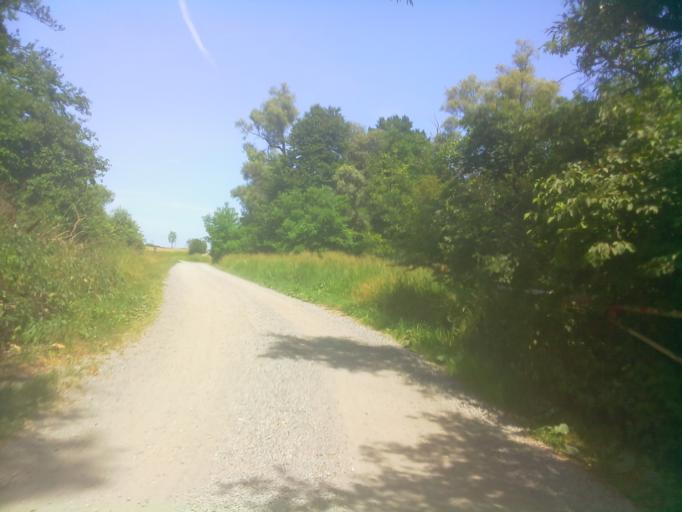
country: DE
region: Hesse
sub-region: Regierungsbezirk Darmstadt
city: Bensheim
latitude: 49.6594
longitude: 8.6119
